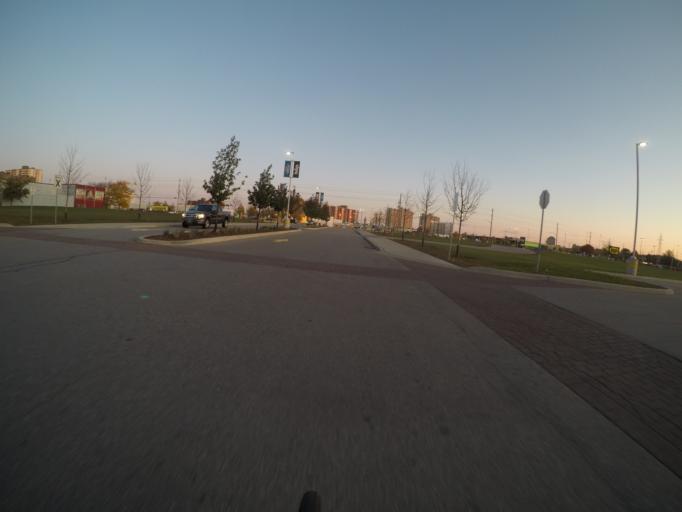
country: CA
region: Ontario
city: Kitchener
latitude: 43.4207
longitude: -80.4391
